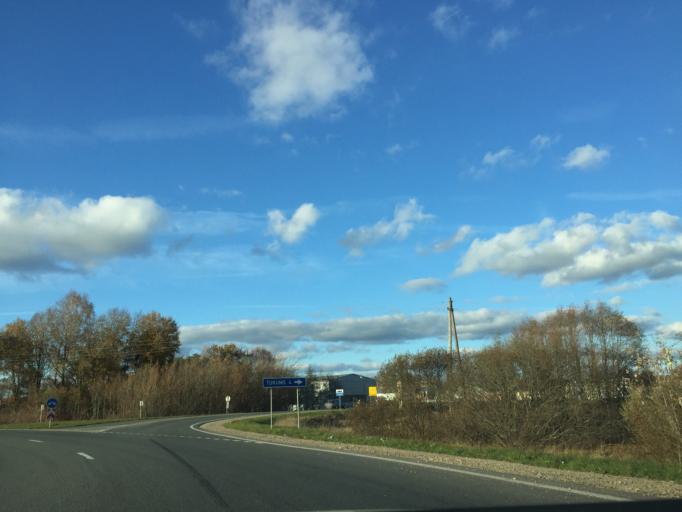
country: LV
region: Tukuma Rajons
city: Tukums
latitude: 56.9493
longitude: 23.1157
